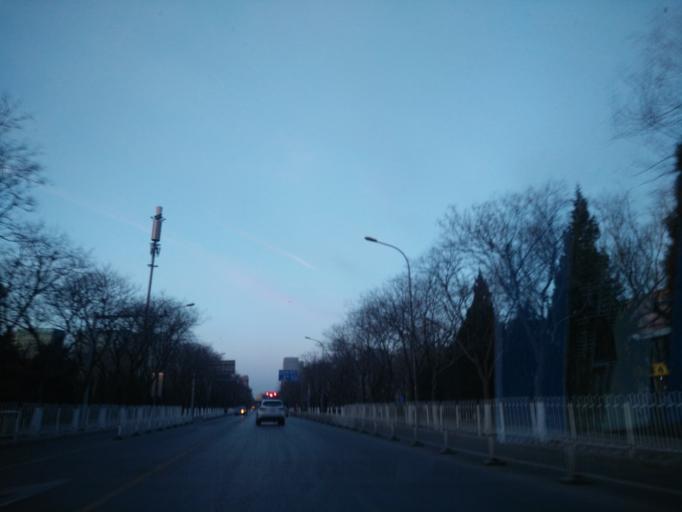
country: CN
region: Beijing
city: Jiugong
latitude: 39.8076
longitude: 116.5004
